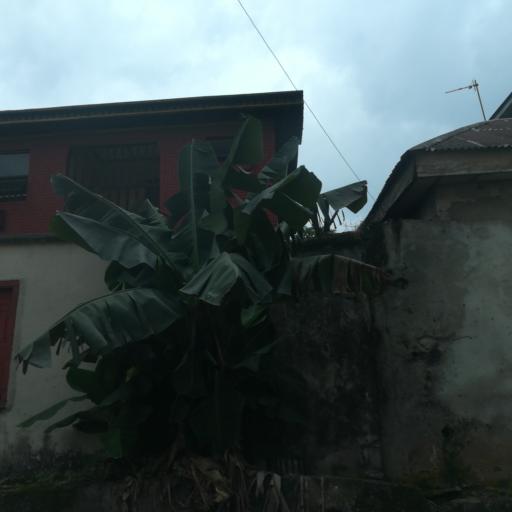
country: NG
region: Rivers
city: Port Harcourt
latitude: 4.8252
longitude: 7.0418
